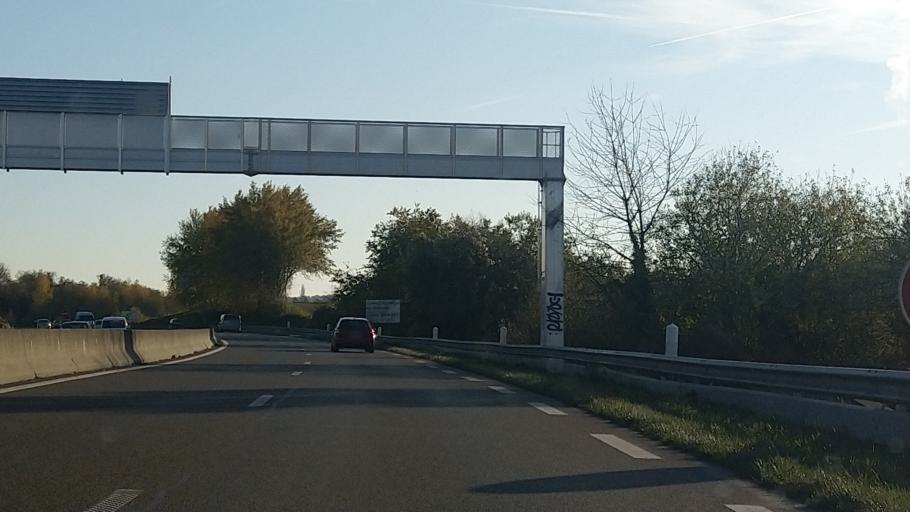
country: FR
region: Ile-de-France
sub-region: Departement du Val-d'Oise
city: Moisselles
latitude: 49.0513
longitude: 2.3301
